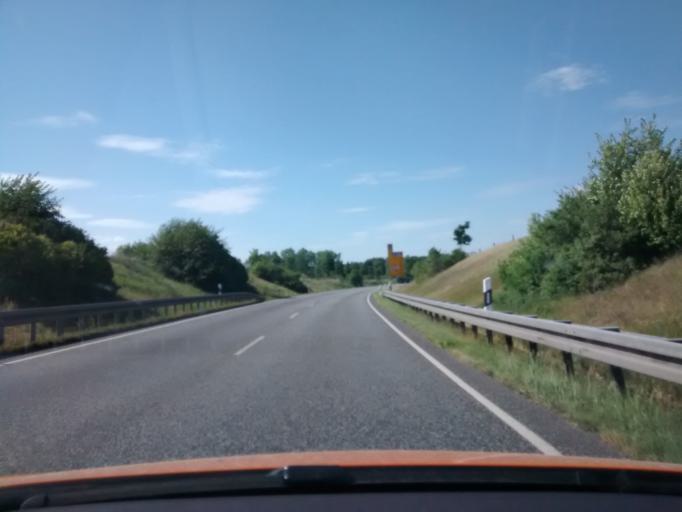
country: DE
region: Brandenburg
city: Juterbog
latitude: 52.0059
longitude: 13.0982
